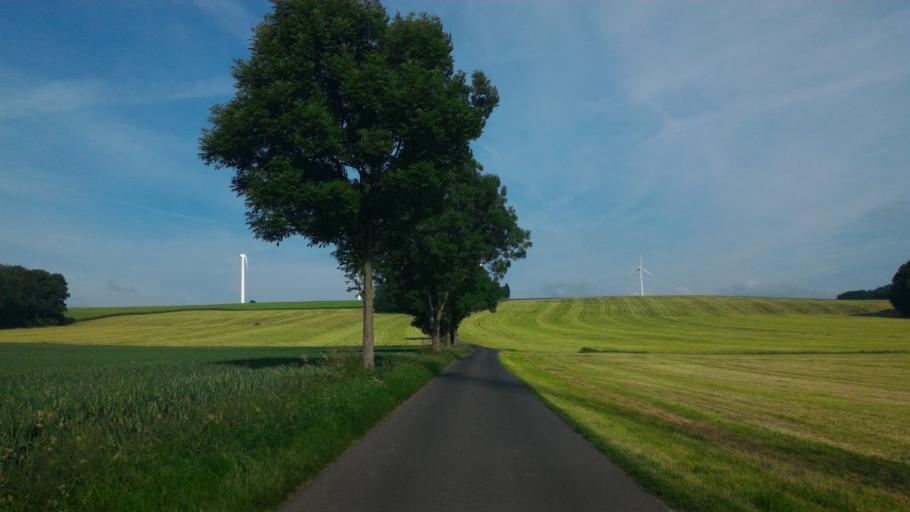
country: DE
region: Saxony
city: Leutersdorf
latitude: 50.9590
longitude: 14.6413
